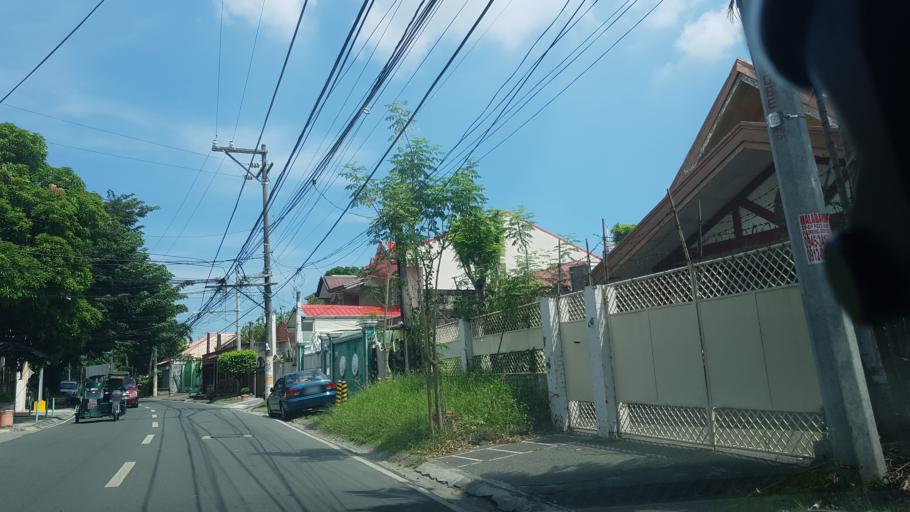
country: PH
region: Calabarzon
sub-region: Province of Rizal
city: Las Pinas
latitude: 14.4331
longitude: 120.9943
